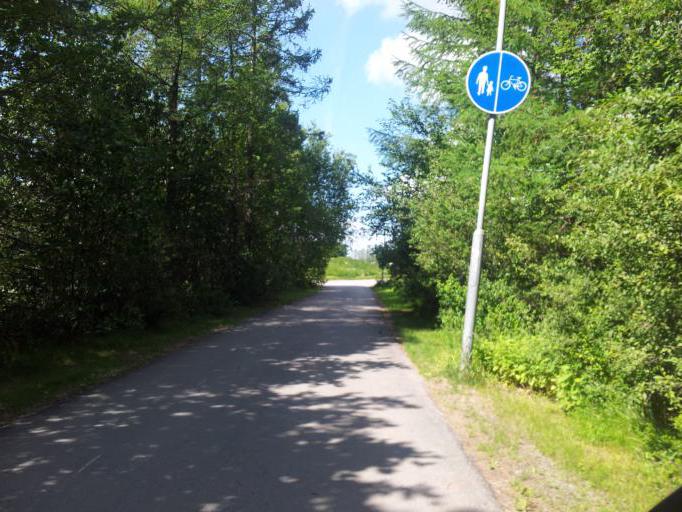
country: SE
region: Uppsala
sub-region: Uppsala Kommun
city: Uppsala
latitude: 59.8788
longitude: 17.6606
